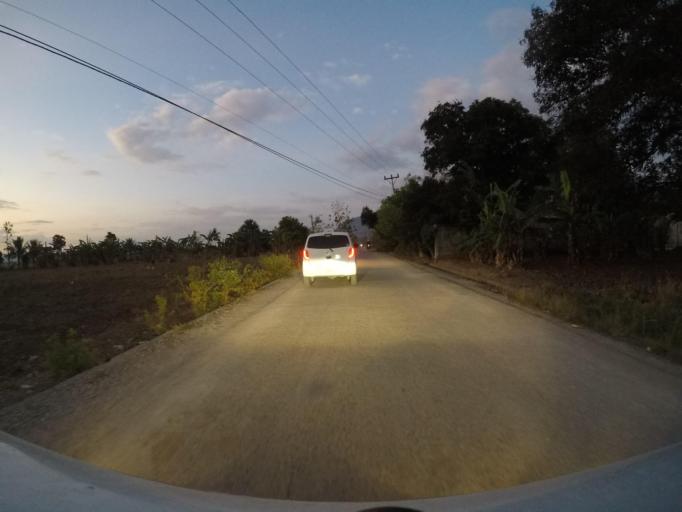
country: TL
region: Bobonaro
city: Maliana
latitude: -8.9882
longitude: 125.2086
